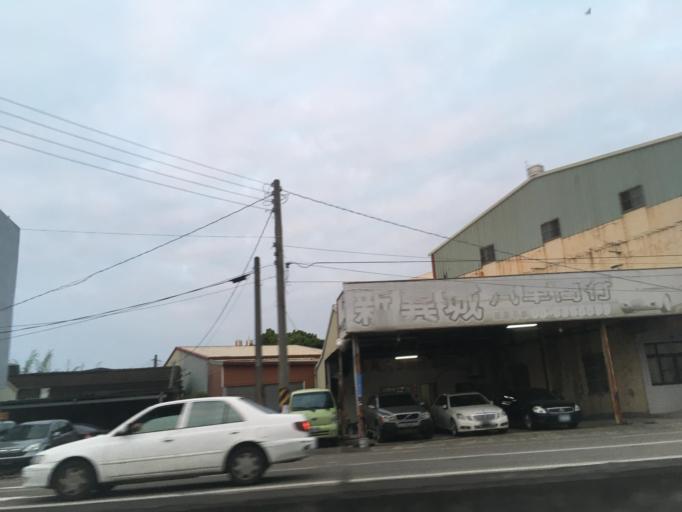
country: TW
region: Taiwan
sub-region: Yunlin
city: Douliu
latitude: 23.7046
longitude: 120.4551
